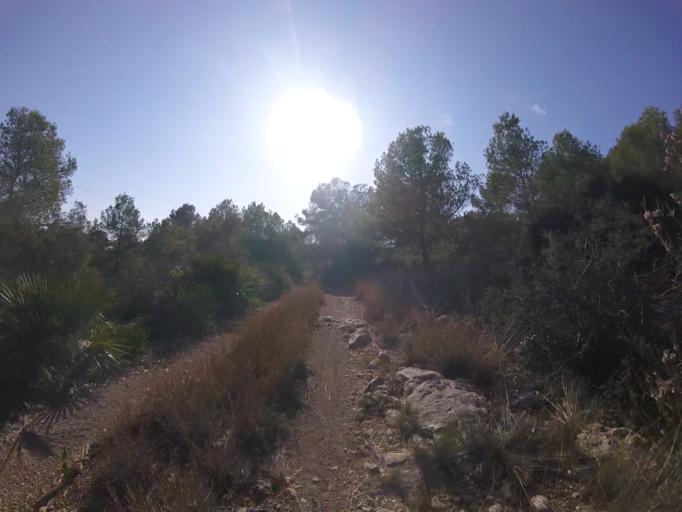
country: ES
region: Valencia
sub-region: Provincia de Castello
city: Santa Magdalena de Pulpis
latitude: 40.3035
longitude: 0.3334
